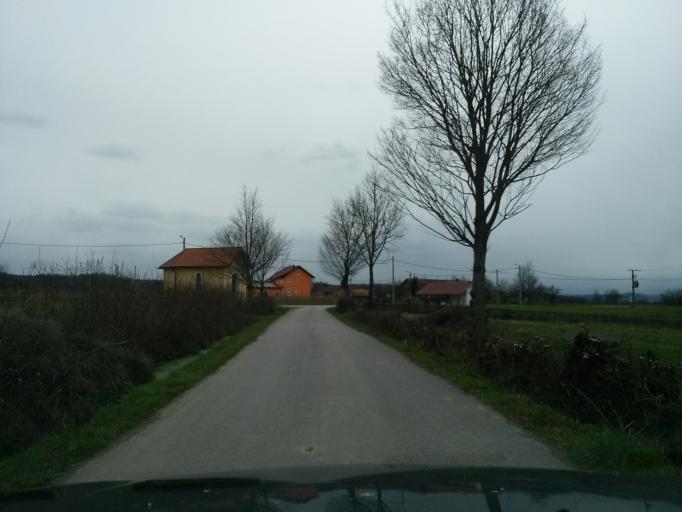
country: HR
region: Sisacko-Moslavacka
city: Gvozd
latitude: 45.2787
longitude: 15.9582
